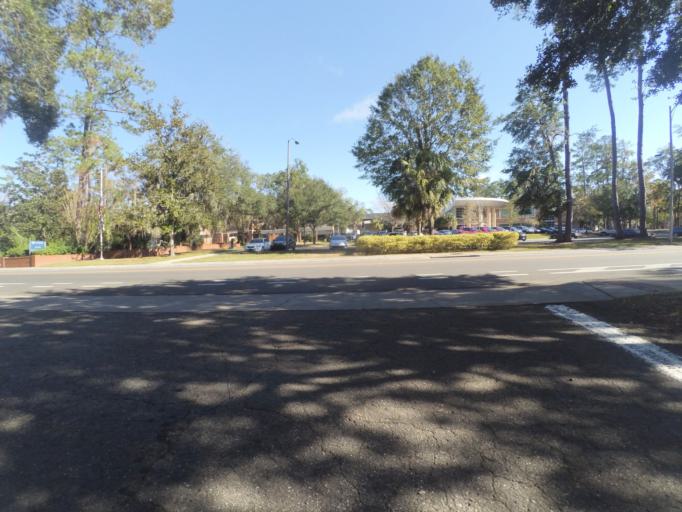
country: US
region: Florida
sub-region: Alachua County
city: Gainesville
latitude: 29.6491
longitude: -82.3605
